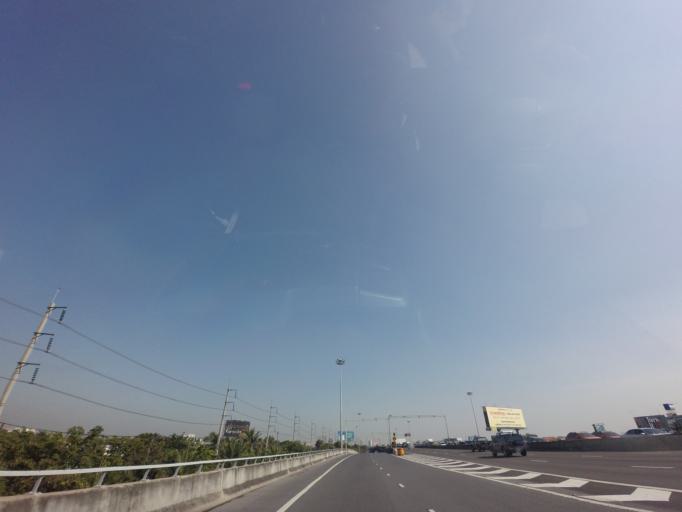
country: TH
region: Bangkok
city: Lat Phrao
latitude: 13.8151
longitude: 100.6223
